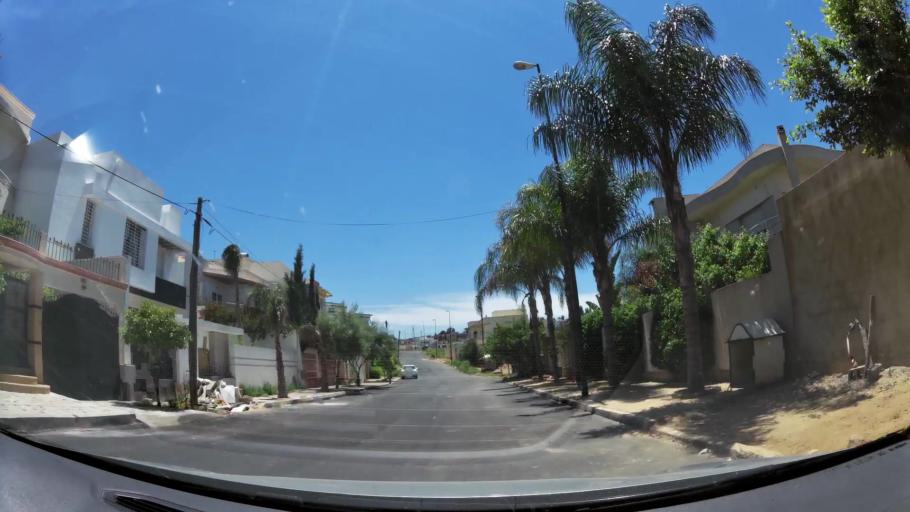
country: MA
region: Meknes-Tafilalet
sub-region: Meknes
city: Meknes
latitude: 33.9083
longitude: -5.5555
